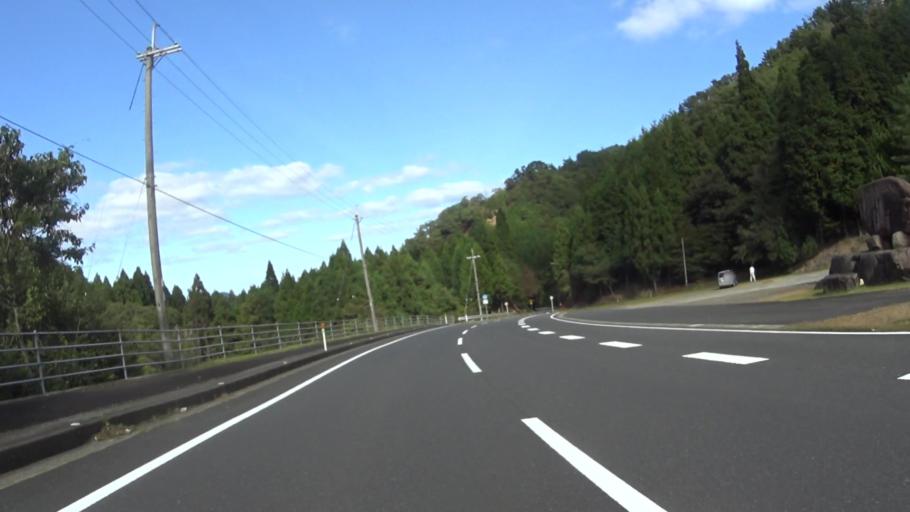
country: JP
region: Hyogo
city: Toyooka
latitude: 35.5339
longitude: 134.9778
